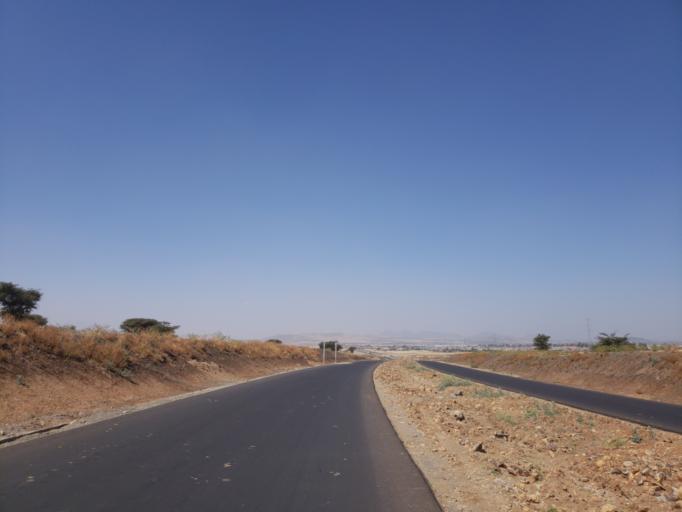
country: ET
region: Oromiya
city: Mojo
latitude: 8.5653
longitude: 39.1539
